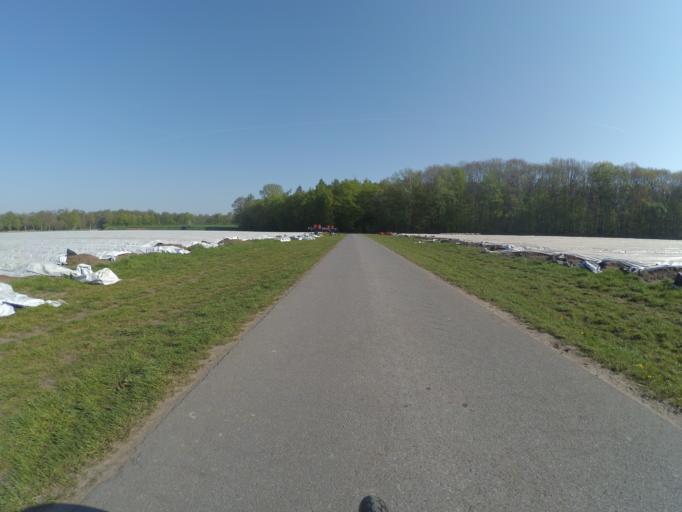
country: DE
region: North Rhine-Westphalia
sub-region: Regierungsbezirk Munster
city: Senden
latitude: 51.8528
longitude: 7.5121
